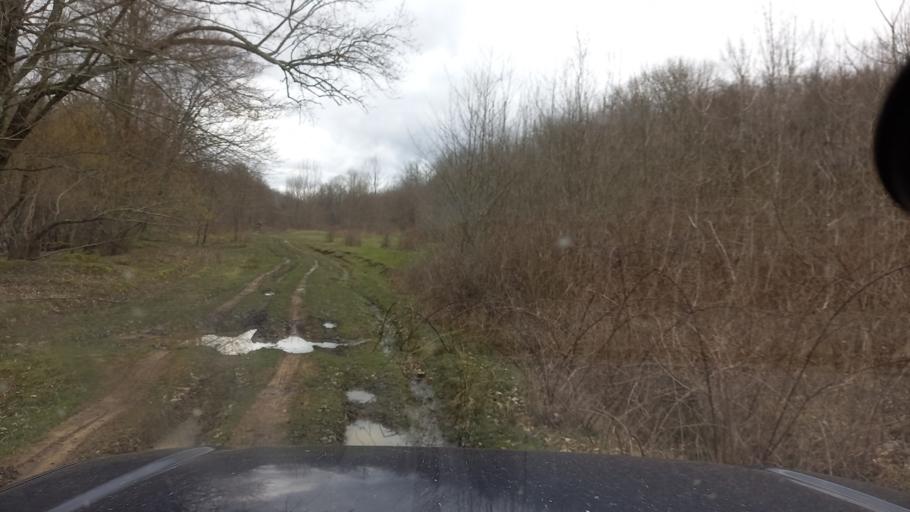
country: RU
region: Krasnodarskiy
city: Pshada
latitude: 44.4858
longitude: 38.3994
